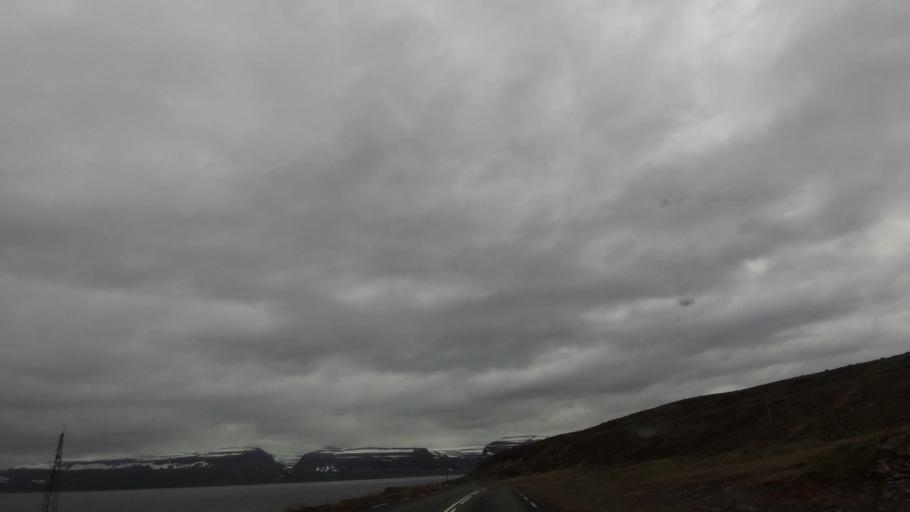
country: IS
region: Westfjords
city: Isafjoerdur
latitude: 66.0478
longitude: -22.7692
